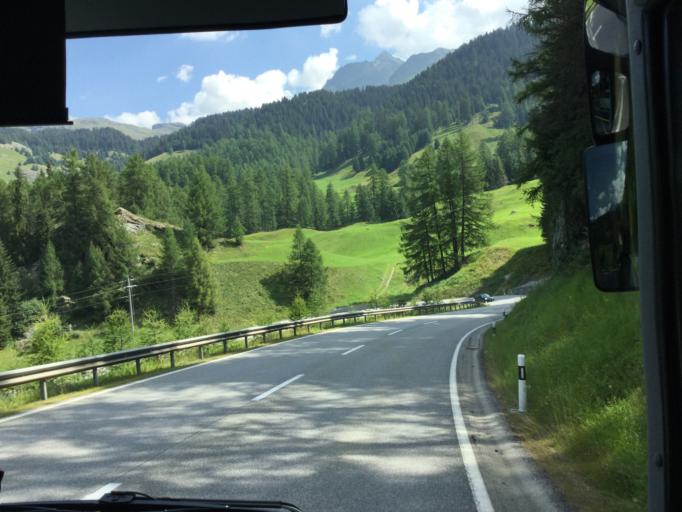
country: CH
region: Grisons
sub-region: Albula District
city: Tiefencastel
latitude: 46.5157
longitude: 9.6288
